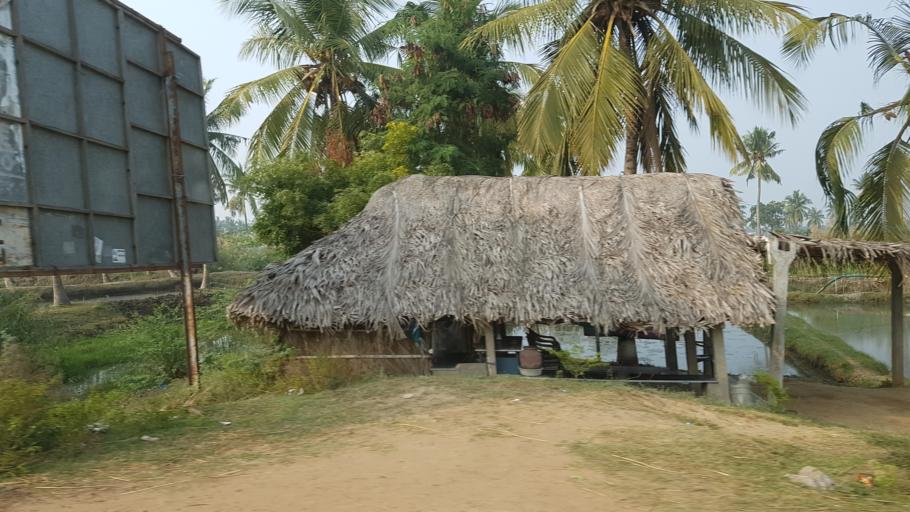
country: IN
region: Andhra Pradesh
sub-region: Krishna
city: Pallevada
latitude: 16.5200
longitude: 81.3344
